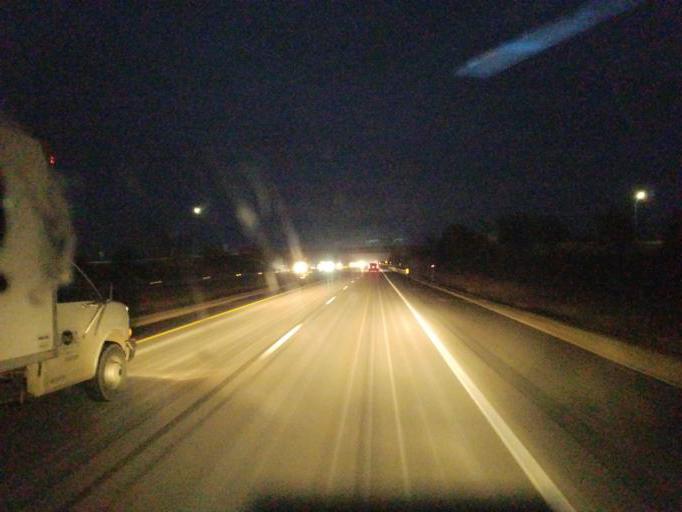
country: US
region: Iowa
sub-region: Guthrie County
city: Stuart
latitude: 41.4958
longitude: -94.4547
